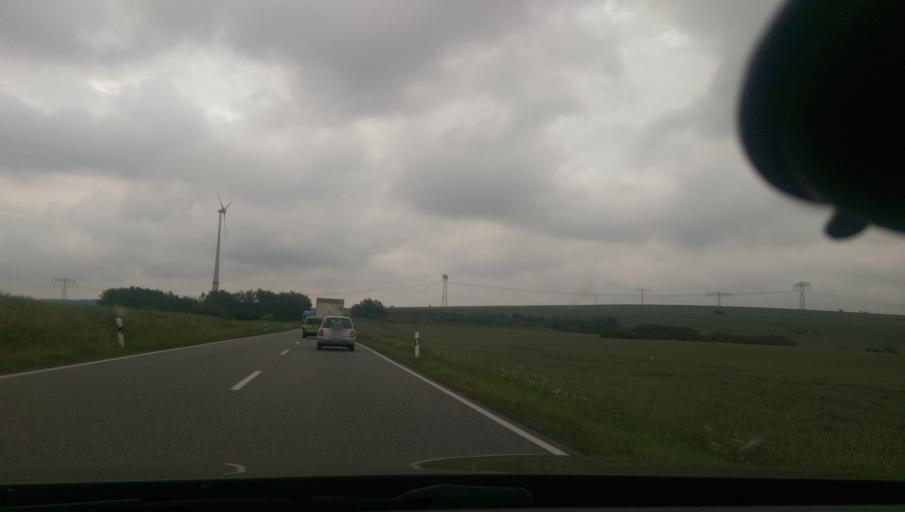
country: DE
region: Thuringia
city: Kleinfurra
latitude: 51.4349
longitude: 10.7919
